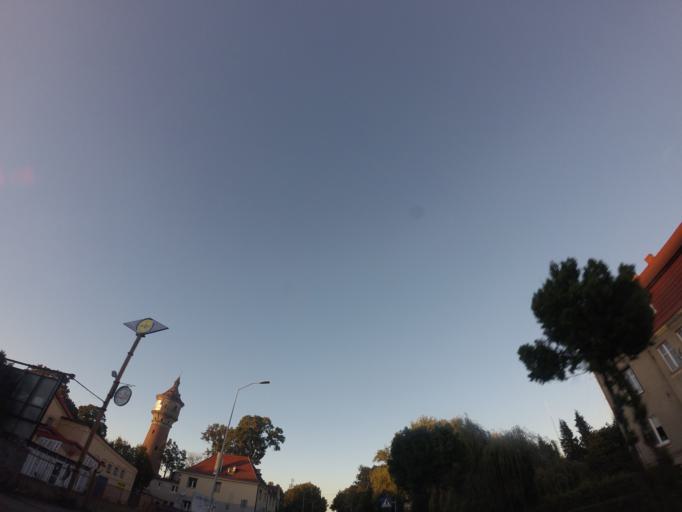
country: PL
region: Lubusz
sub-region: Powiat strzelecko-drezdenecki
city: Drezdenko
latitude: 52.8445
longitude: 15.8325
